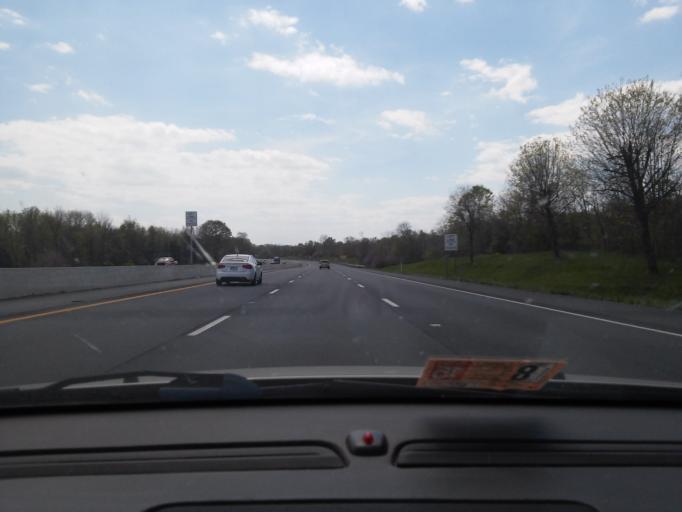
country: US
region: West Virginia
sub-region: Berkeley County
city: Martinsburg
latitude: 39.5301
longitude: -77.9243
